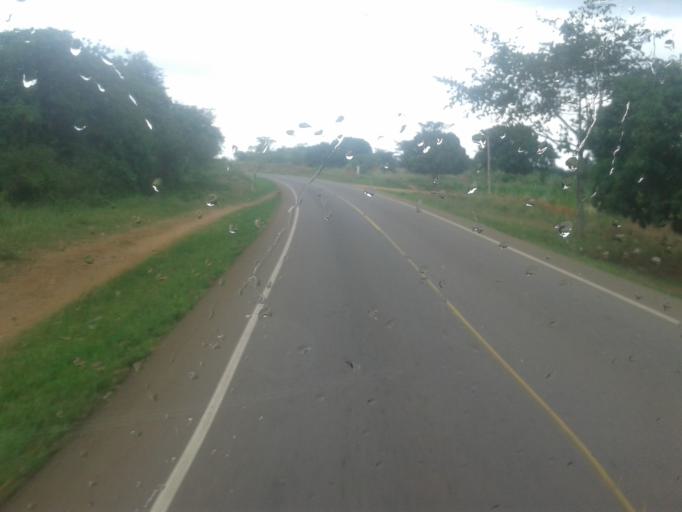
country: UG
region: Central Region
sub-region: Nakasongola District
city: Nakasongola
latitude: 1.3234
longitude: 32.4221
